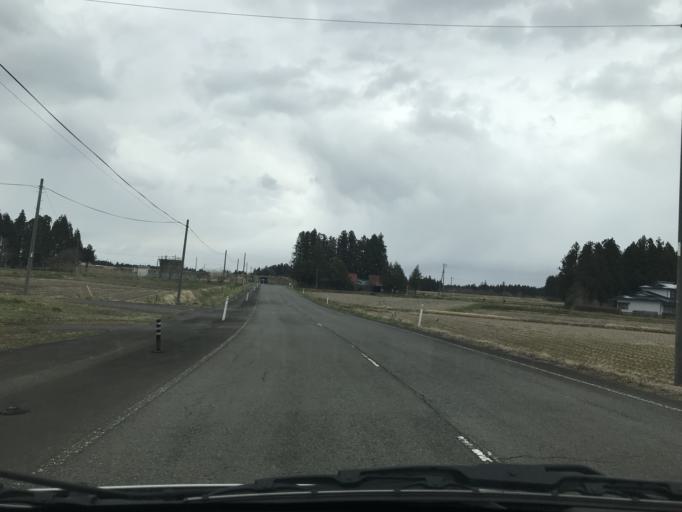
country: JP
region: Iwate
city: Mizusawa
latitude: 39.0711
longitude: 141.0770
